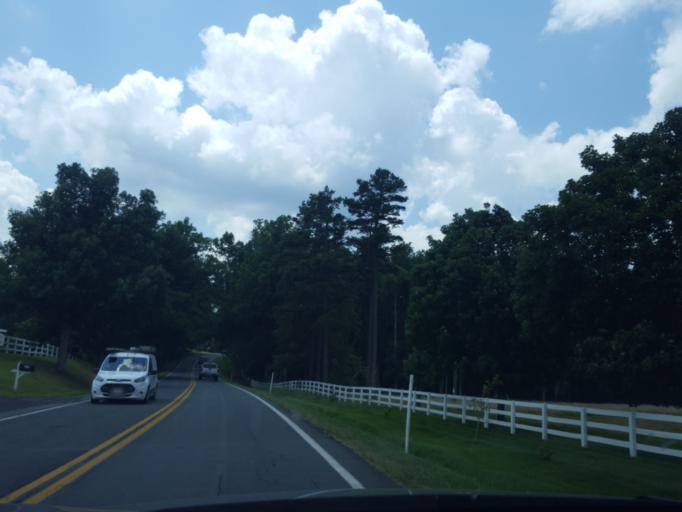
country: US
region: Virginia
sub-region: Orange County
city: Gordonsville
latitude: 38.0758
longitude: -78.2934
